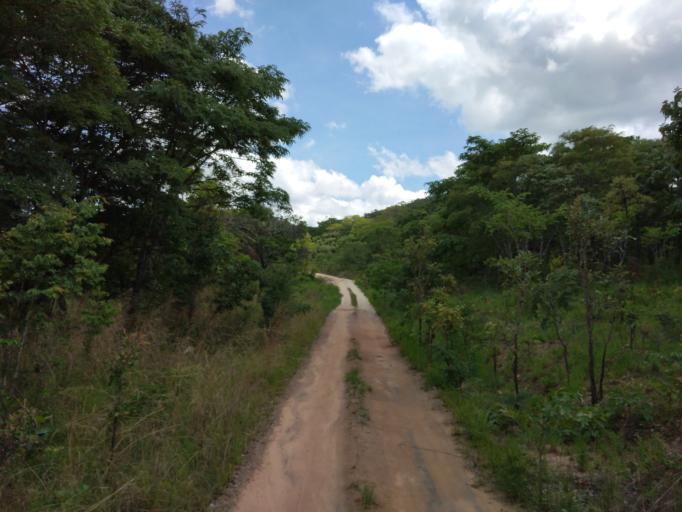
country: ZM
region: Central
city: Mkushi
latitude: -13.9785
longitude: 29.9407
